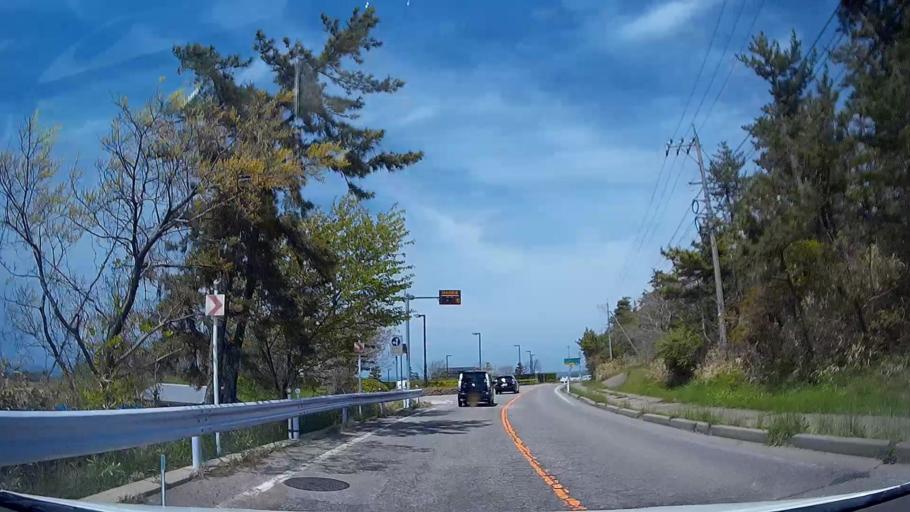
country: JP
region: Ishikawa
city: Hakui
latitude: 36.9323
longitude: 136.7562
